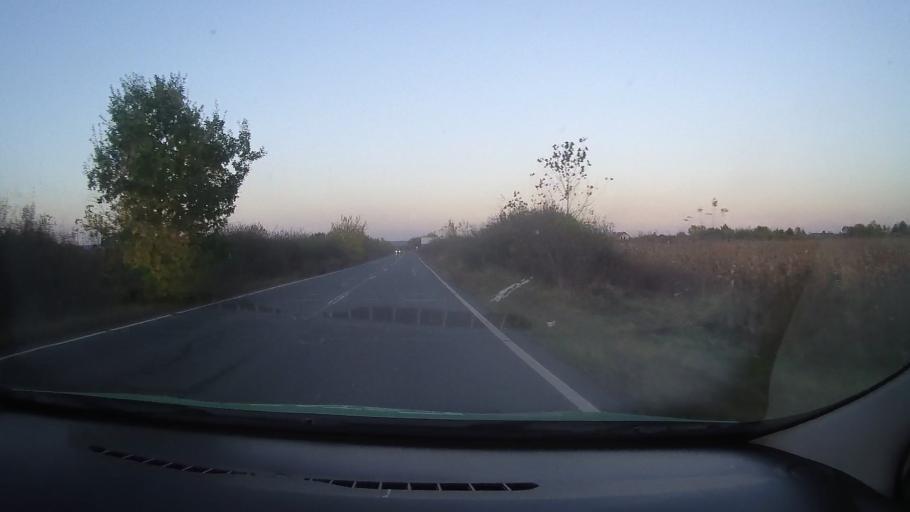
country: RO
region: Timis
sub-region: Comuna Dumbrava
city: Dumbrava
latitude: 45.8361
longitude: 22.1398
